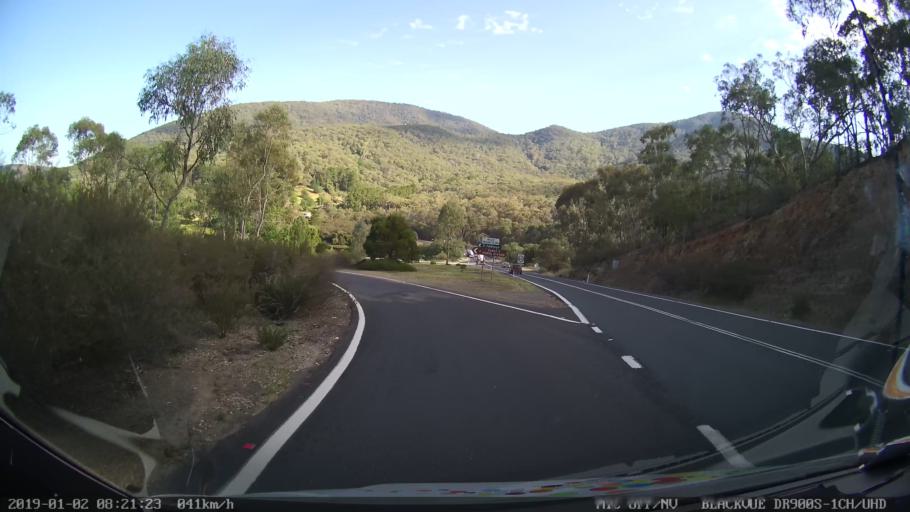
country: AU
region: New South Wales
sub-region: Tumut Shire
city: Tumut
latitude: -35.5692
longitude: 148.3257
